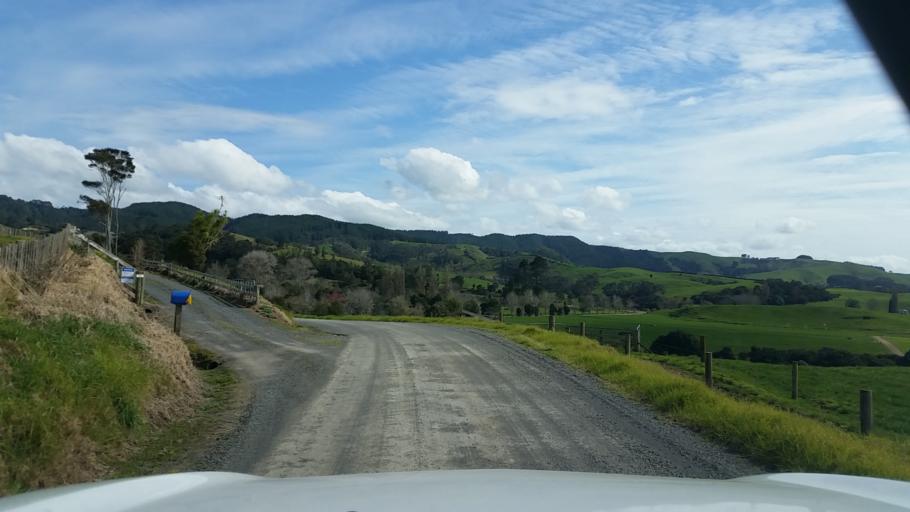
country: NZ
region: Waikato
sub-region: Hauraki District
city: Ngatea
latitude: -37.4469
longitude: 175.4930
